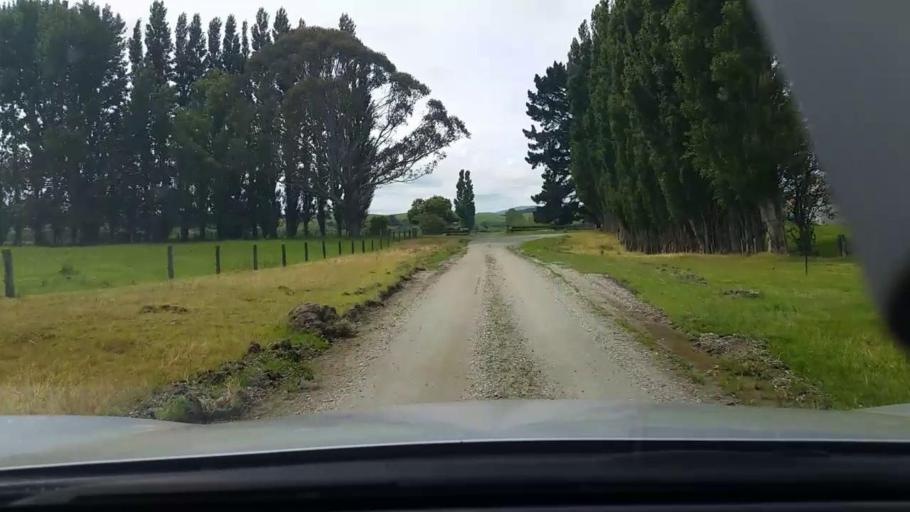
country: NZ
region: Southland
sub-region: Gore District
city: Gore
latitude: -46.1550
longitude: 168.9077
